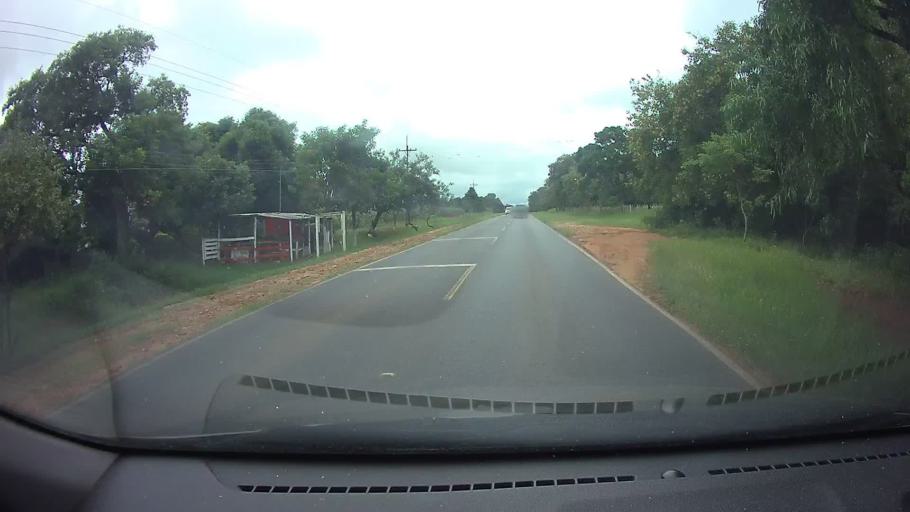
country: PY
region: Central
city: Nueva Italia
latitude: -25.5805
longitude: -57.5059
